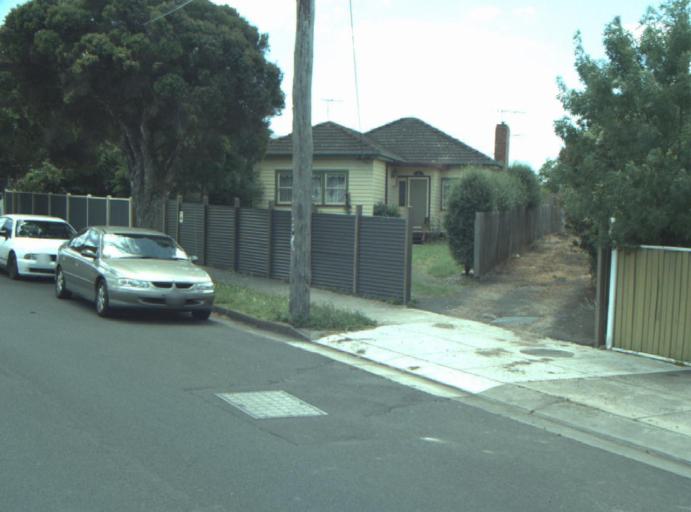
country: AU
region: Victoria
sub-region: Greater Geelong
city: Breakwater
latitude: -38.1771
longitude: 144.3441
